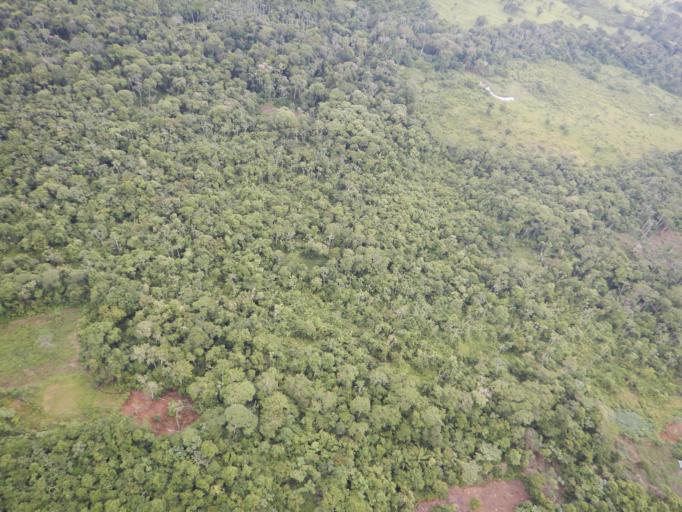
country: BO
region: Santa Cruz
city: Villa Yapacani
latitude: -17.3074
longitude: -64.1080
